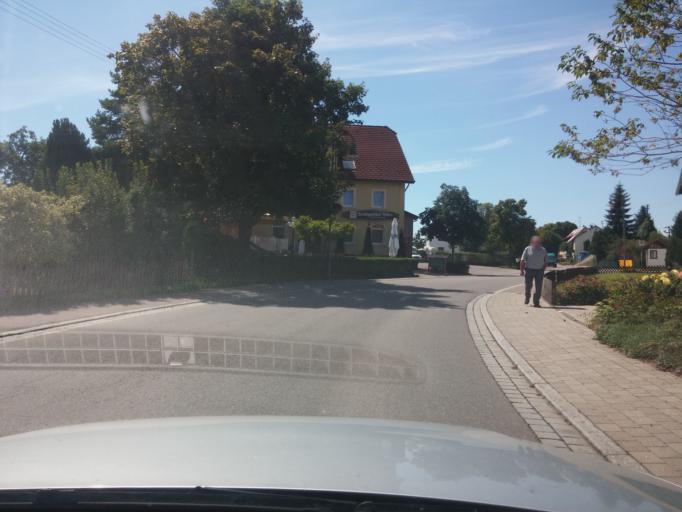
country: DE
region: Baden-Wuerttemberg
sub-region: Tuebingen Region
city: Illmensee
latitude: 47.8611
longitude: 9.3733
